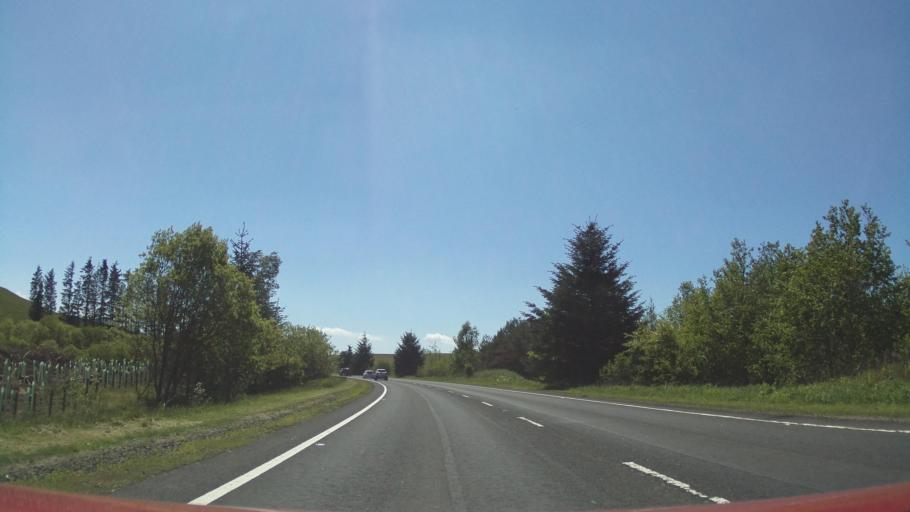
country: GB
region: Scotland
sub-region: The Scottish Borders
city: Selkirk
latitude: 55.5138
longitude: -2.8465
